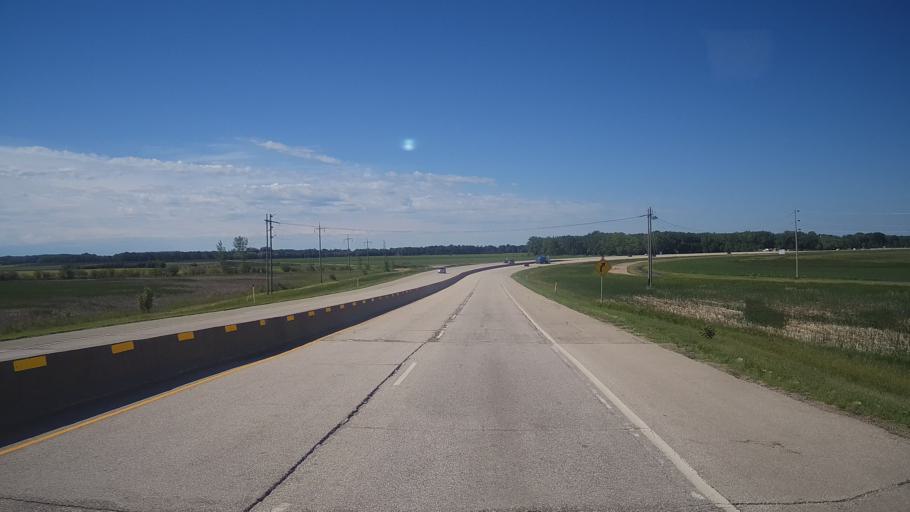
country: CA
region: Manitoba
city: Portage la Prairie
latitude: 49.9655
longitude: -98.2362
